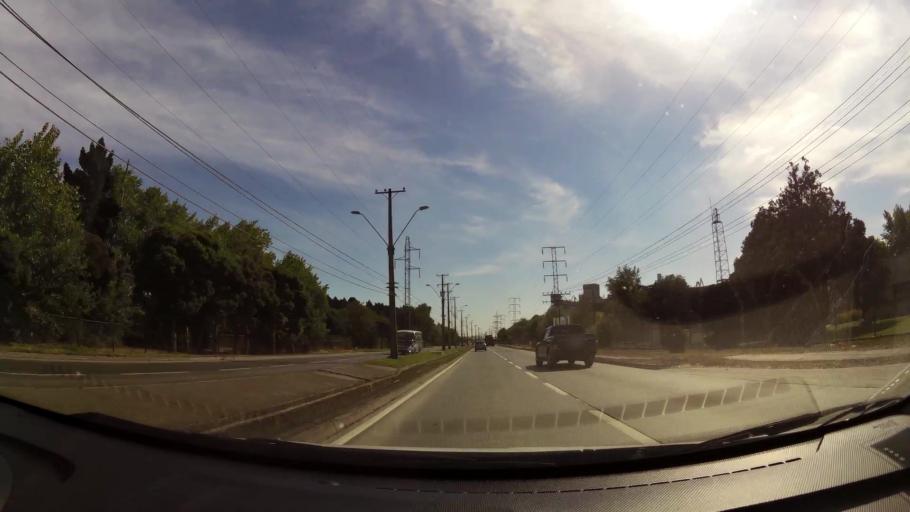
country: CL
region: Biobio
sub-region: Provincia de Concepcion
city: Talcahuano
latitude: -36.7453
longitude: -73.1219
